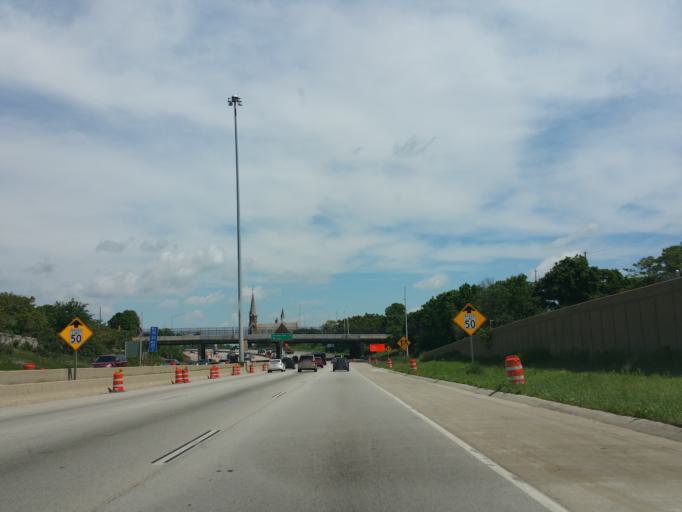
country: US
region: Wisconsin
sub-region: Milwaukee County
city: Milwaukee
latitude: 43.0151
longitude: -87.9159
